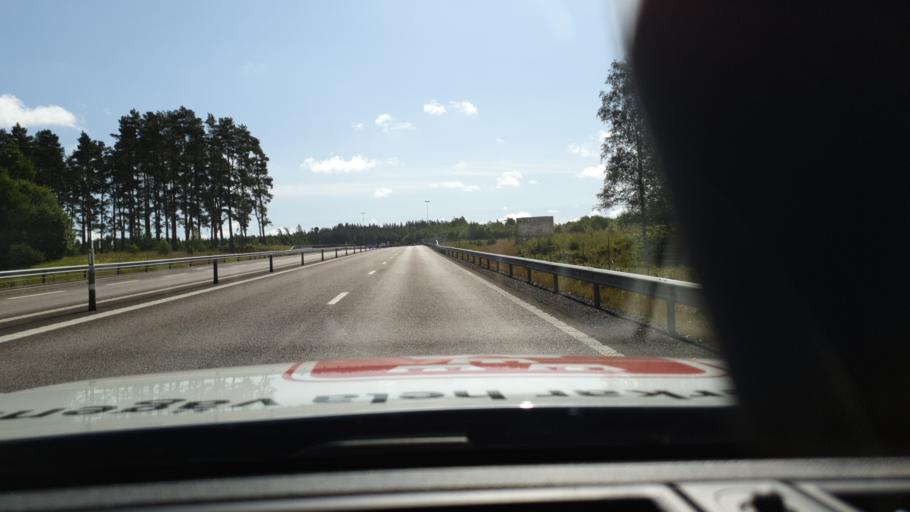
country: SE
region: Joenkoeping
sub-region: Jonkopings Kommun
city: Tenhult
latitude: 57.7188
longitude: 14.3752
